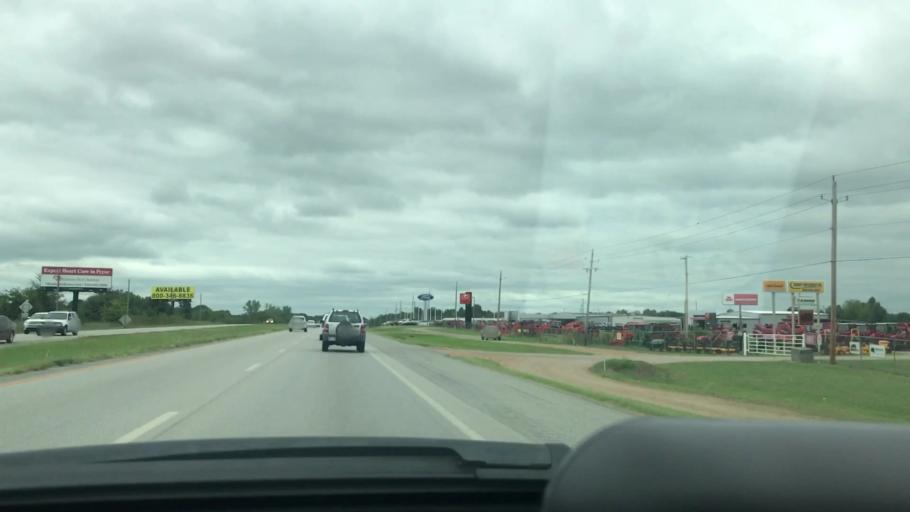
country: US
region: Oklahoma
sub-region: Mayes County
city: Pryor
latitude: 36.2648
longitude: -95.3328
